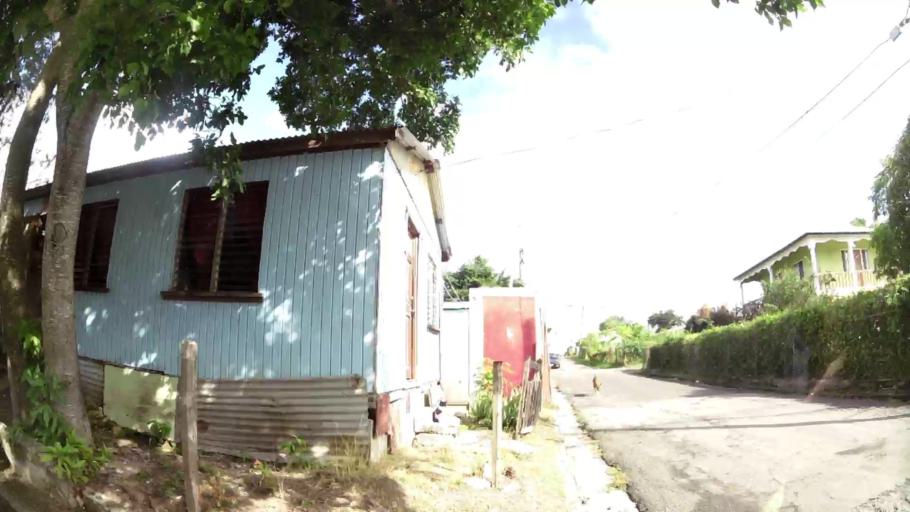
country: AG
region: Saint John
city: Saint John's
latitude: 17.1201
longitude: -61.8303
